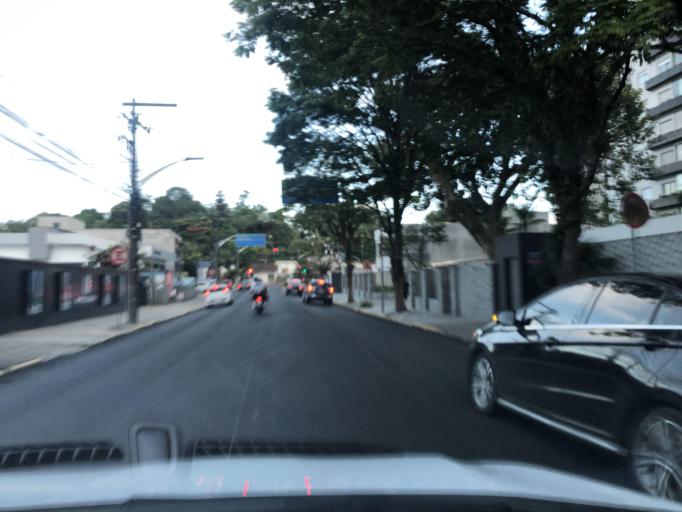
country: BR
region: Santa Catarina
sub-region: Joinville
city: Joinville
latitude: -26.2988
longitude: -48.8543
